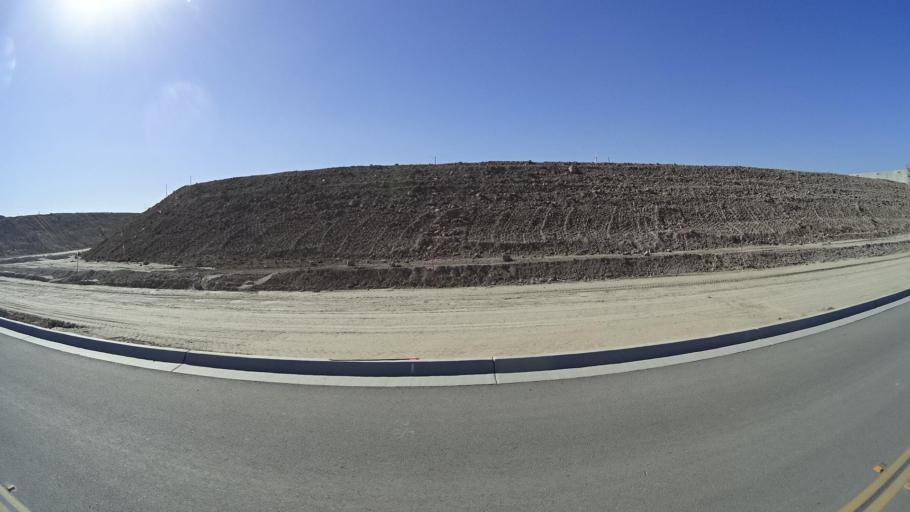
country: MX
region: Baja California
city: Tijuana
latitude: 32.5711
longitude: -116.9217
